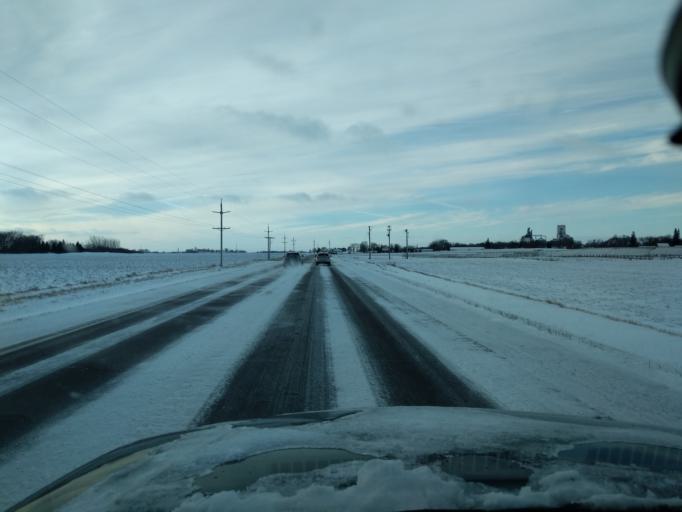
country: US
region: Minnesota
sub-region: Renville County
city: Hector
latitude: 44.7314
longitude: -94.6051
